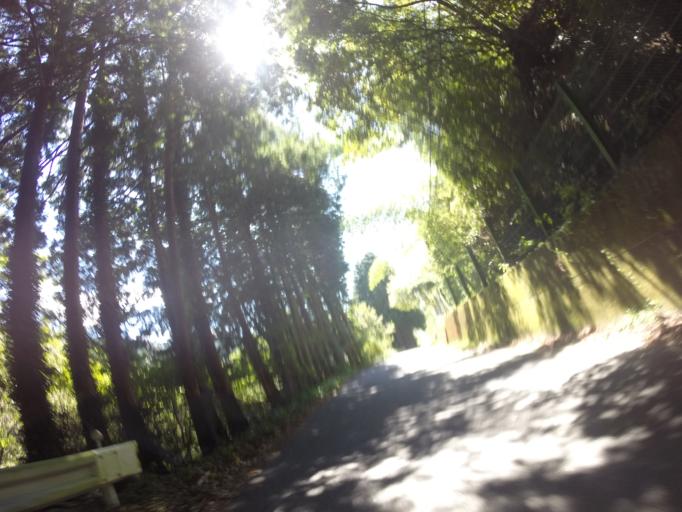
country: JP
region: Shizuoka
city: Fujieda
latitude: 34.9712
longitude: 138.2118
